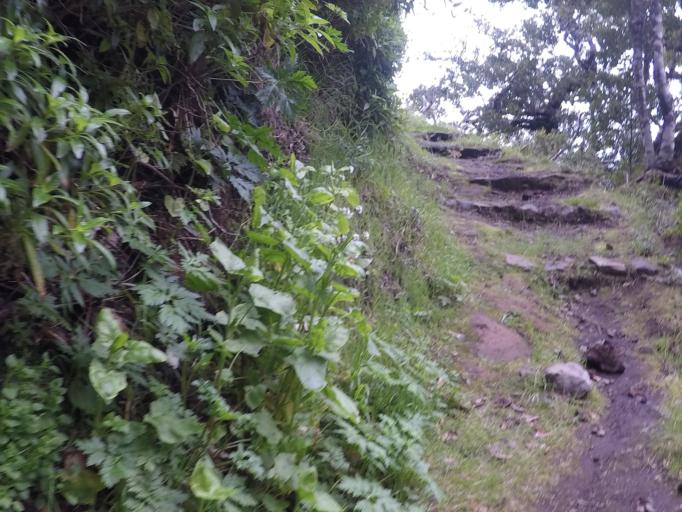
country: PT
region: Madeira
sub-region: Camara de Lobos
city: Curral das Freiras
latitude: 32.7351
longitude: -16.9924
